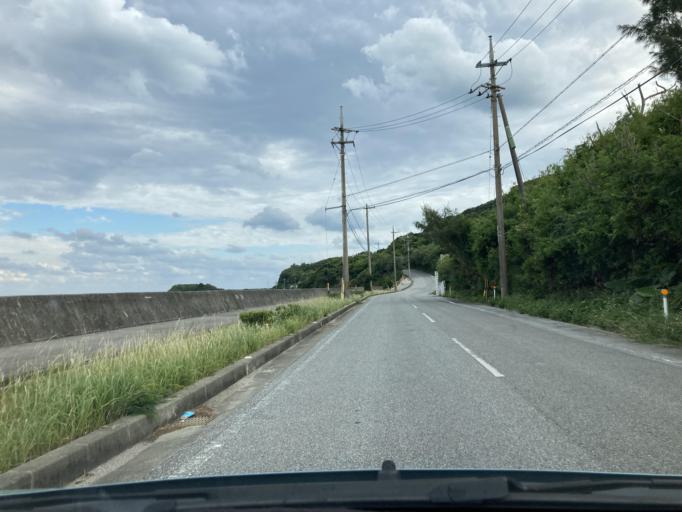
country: JP
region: Okinawa
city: Katsuren-haebaru
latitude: 26.3275
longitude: 127.9583
